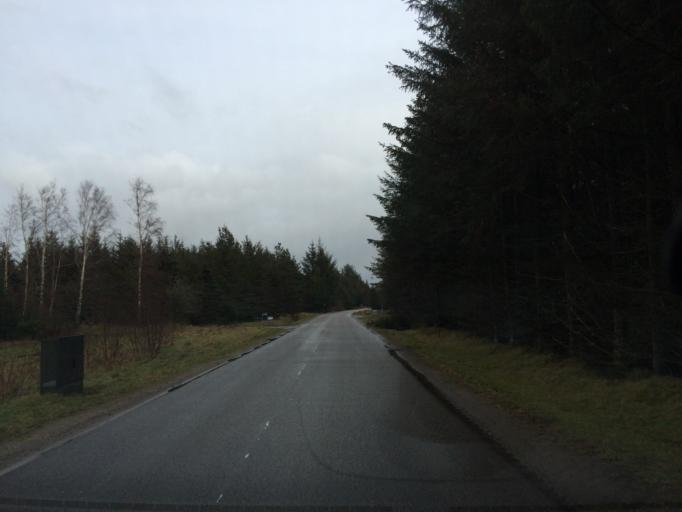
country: DK
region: Central Jutland
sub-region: Holstebro Kommune
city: Ulfborg
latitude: 56.2778
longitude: 8.1610
